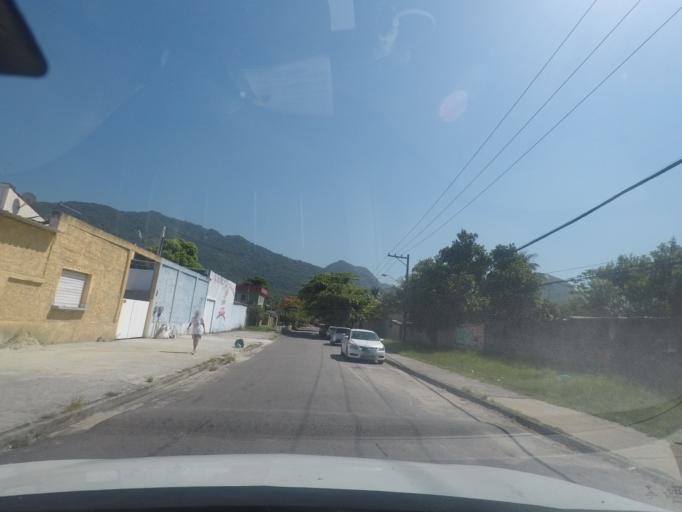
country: BR
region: Rio de Janeiro
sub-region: Nilopolis
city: Nilopolis
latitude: -22.9863
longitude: -43.4570
